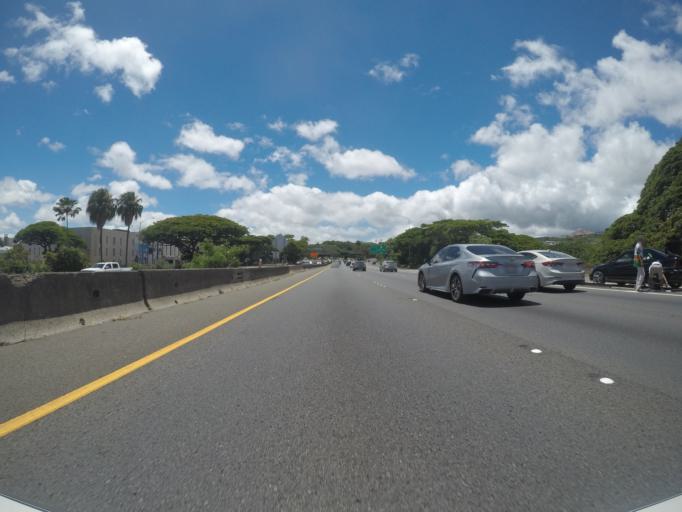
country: US
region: Hawaii
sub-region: Honolulu County
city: Halawa Heights
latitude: 21.3454
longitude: -157.8933
